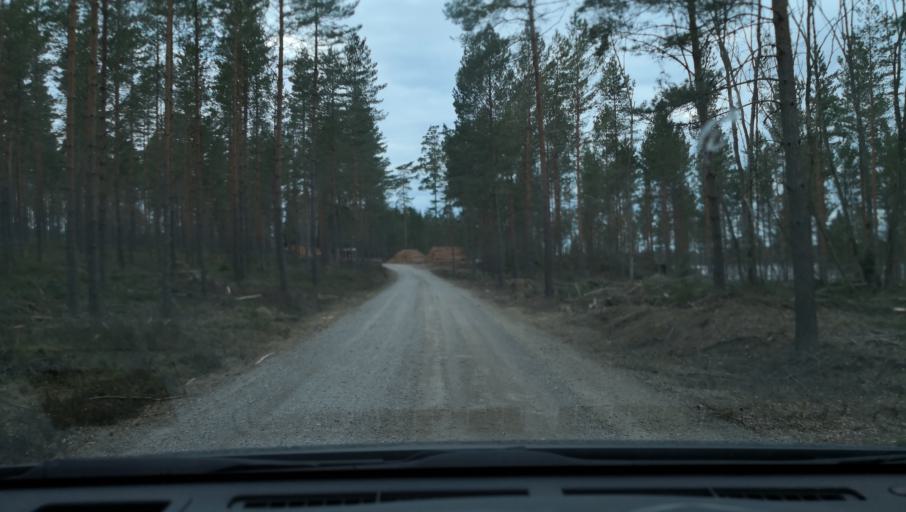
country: SE
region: Soedermanland
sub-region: Katrineholms Kommun
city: Katrineholm
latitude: 59.1347
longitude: 16.1440
